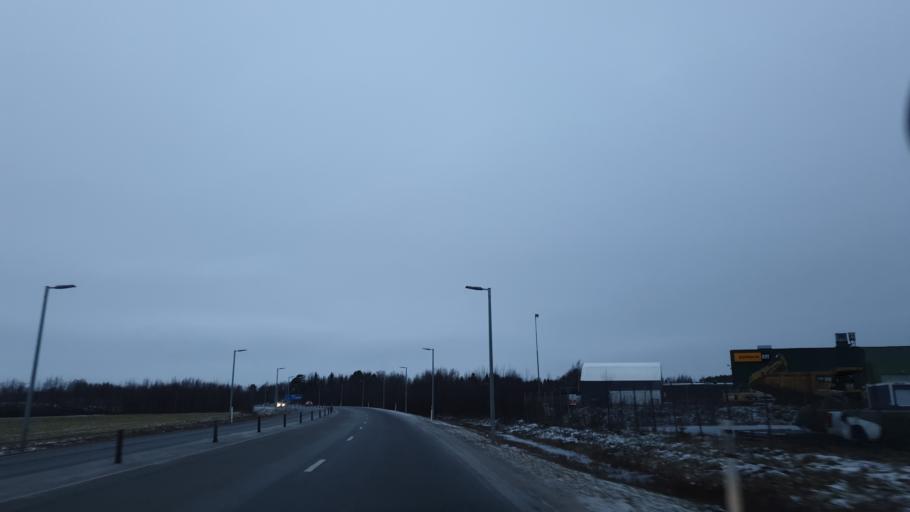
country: SE
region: Vaesterbotten
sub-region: Umea Kommun
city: Umea
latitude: 63.8018
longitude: 20.2675
